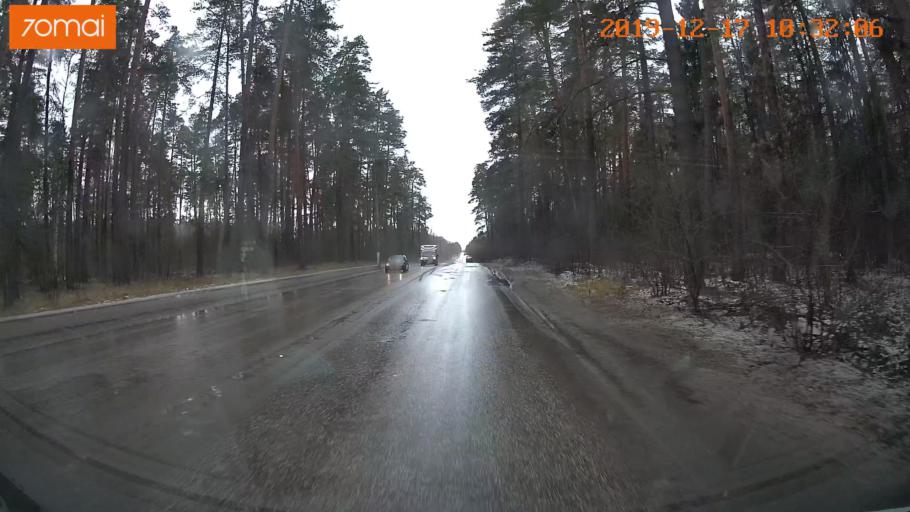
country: RU
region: Vladimir
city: Gus'-Khrustal'nyy
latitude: 55.6310
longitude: 40.6918
